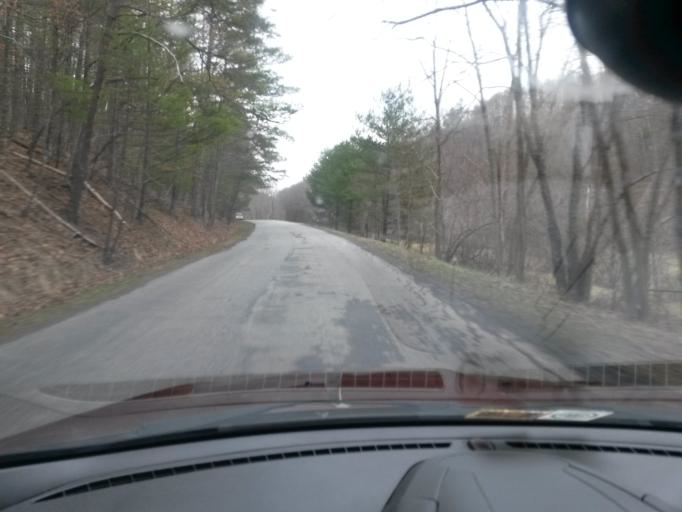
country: US
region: Virginia
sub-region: Bath County
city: Warm Springs
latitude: 38.0267
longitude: -79.8606
